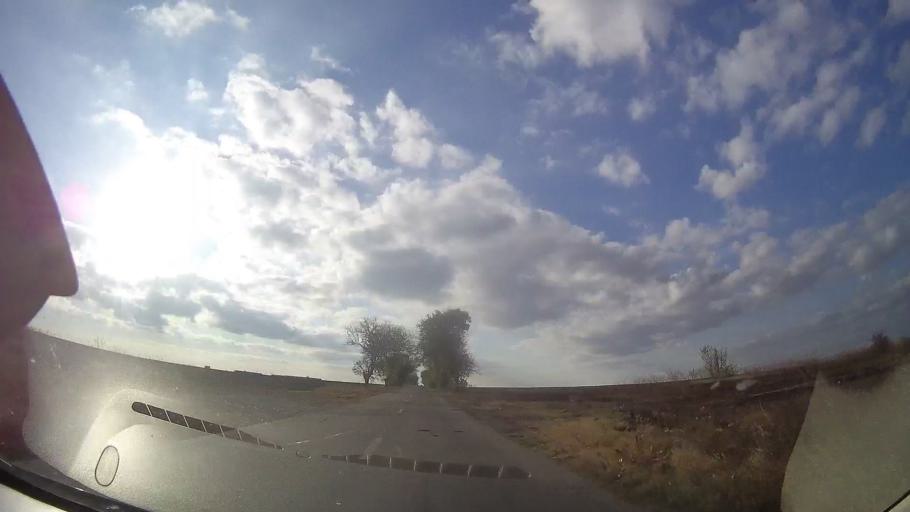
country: RO
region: Constanta
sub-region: Comuna Comana
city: Comana
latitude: 43.8207
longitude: 28.3059
